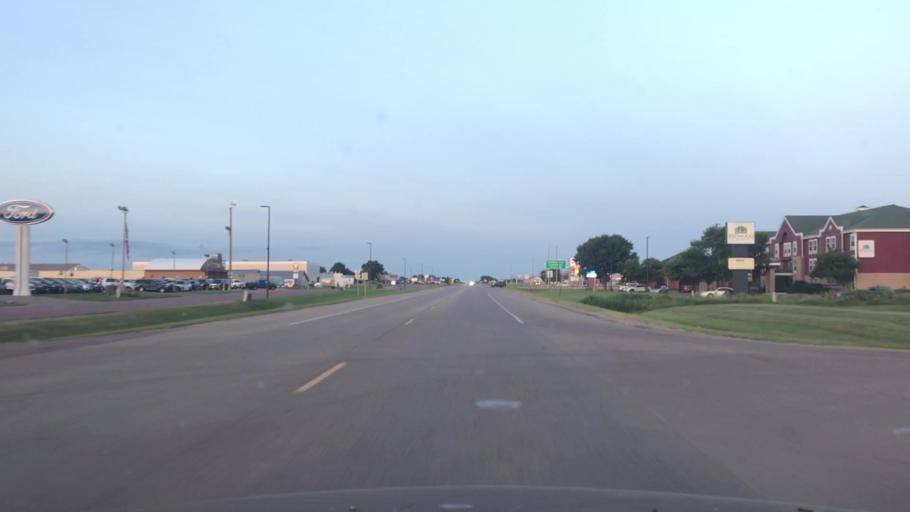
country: US
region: Minnesota
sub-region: Redwood County
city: Redwood Falls
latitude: 44.5413
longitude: -95.0933
